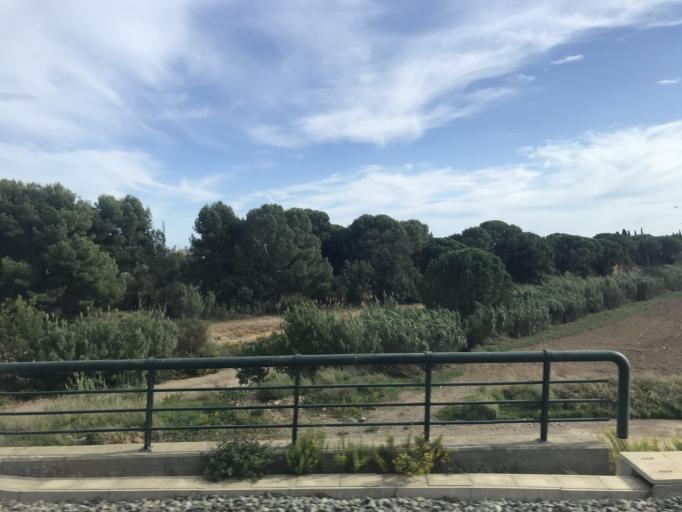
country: ES
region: Catalonia
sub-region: Provincia de Tarragona
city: Cambrils
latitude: 41.0927
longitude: 1.0805
